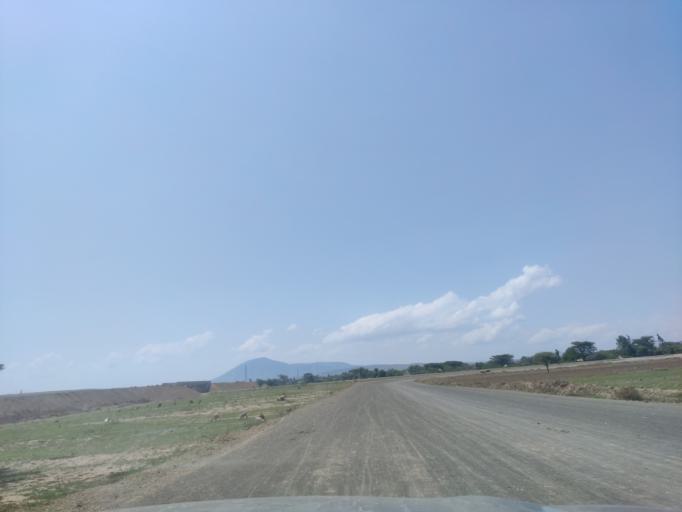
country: ET
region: Oromiya
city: Mojo
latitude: 8.3025
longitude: 38.9328
